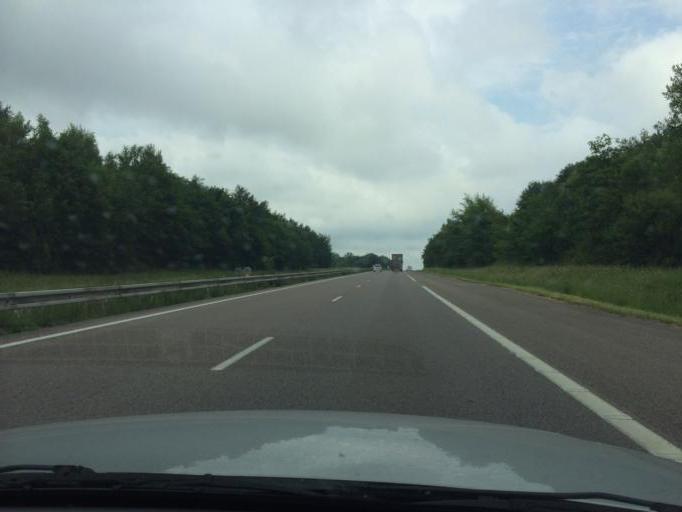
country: FR
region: Picardie
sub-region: Departement de l'Aisne
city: Brasles
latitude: 49.1046
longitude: 3.4603
